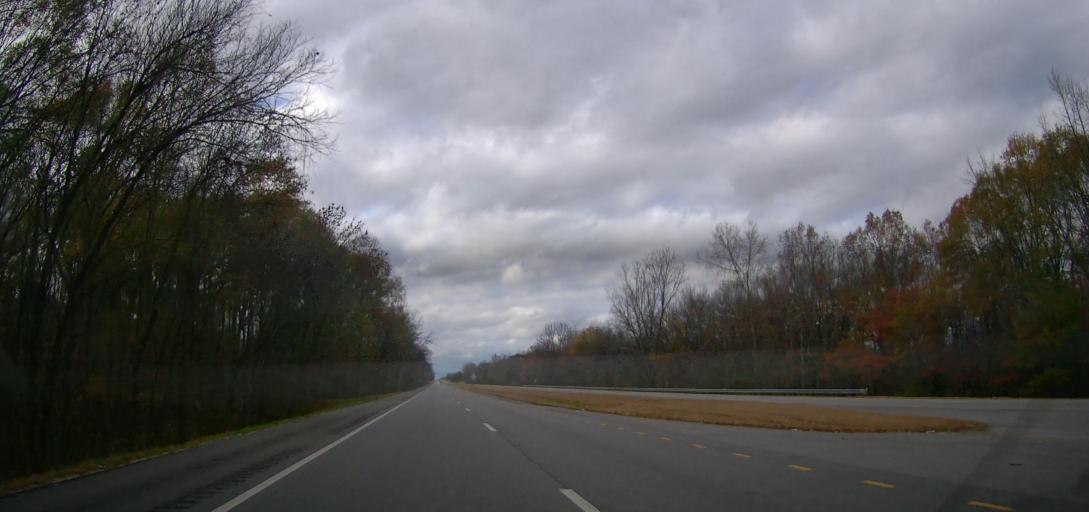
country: US
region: Alabama
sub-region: Lawrence County
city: Town Creek
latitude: 34.6337
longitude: -87.4906
